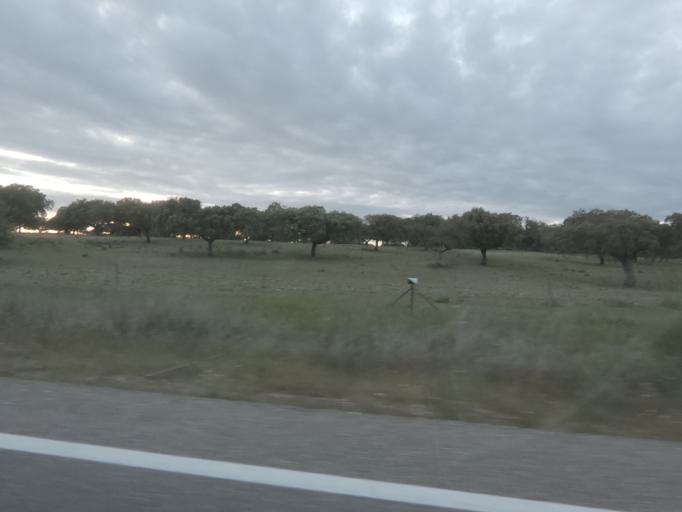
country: ES
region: Extremadura
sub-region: Provincia de Badajoz
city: La Roca de la Sierra
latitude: 39.0728
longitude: -6.7532
